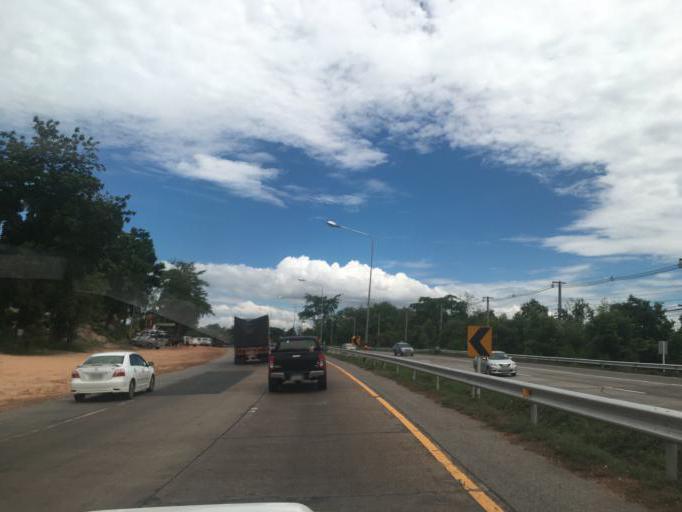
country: TH
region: Khon Kaen
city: Nam Phong
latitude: 16.6585
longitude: 102.8002
